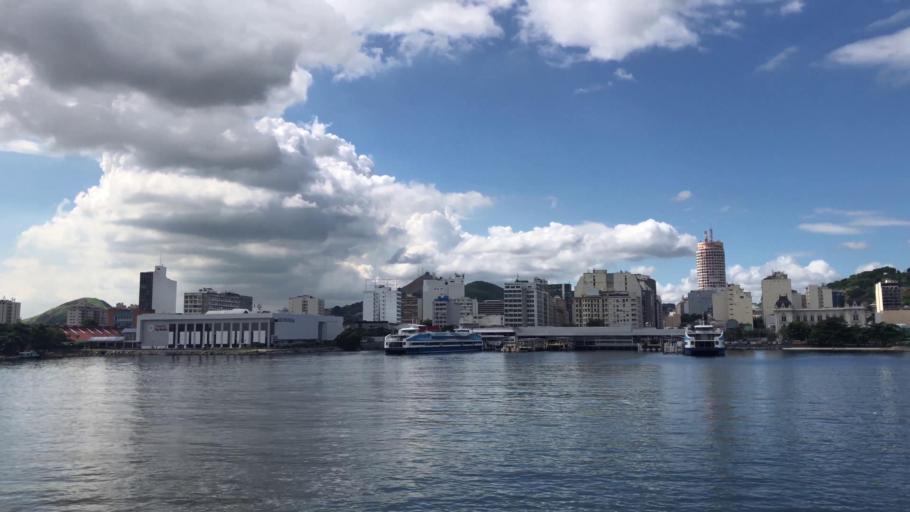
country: BR
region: Rio de Janeiro
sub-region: Niteroi
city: Niteroi
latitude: -22.8925
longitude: -43.1263
